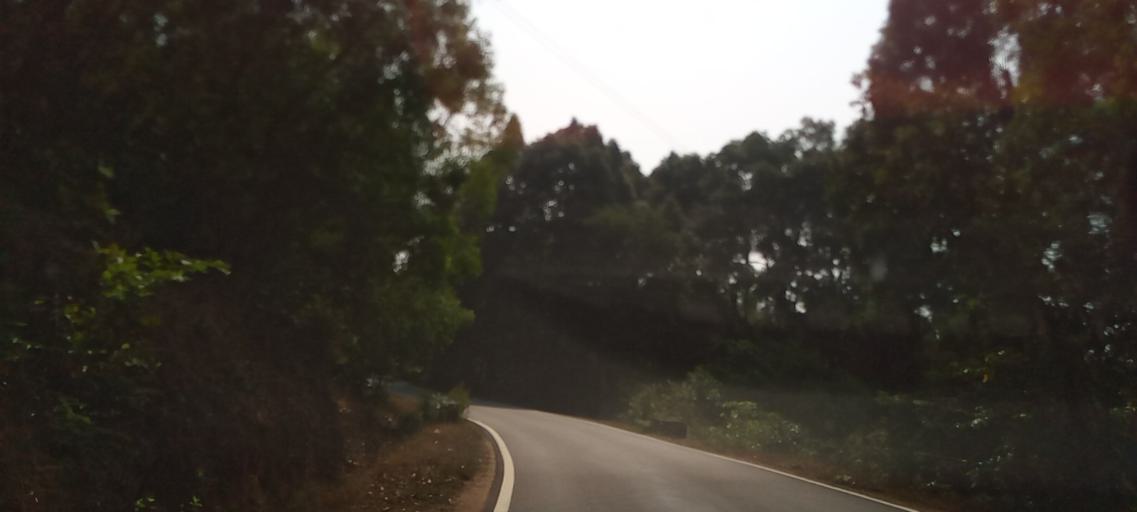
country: IN
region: Karnataka
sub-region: Udupi
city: Hosangadi
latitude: 13.5417
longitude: 74.9044
